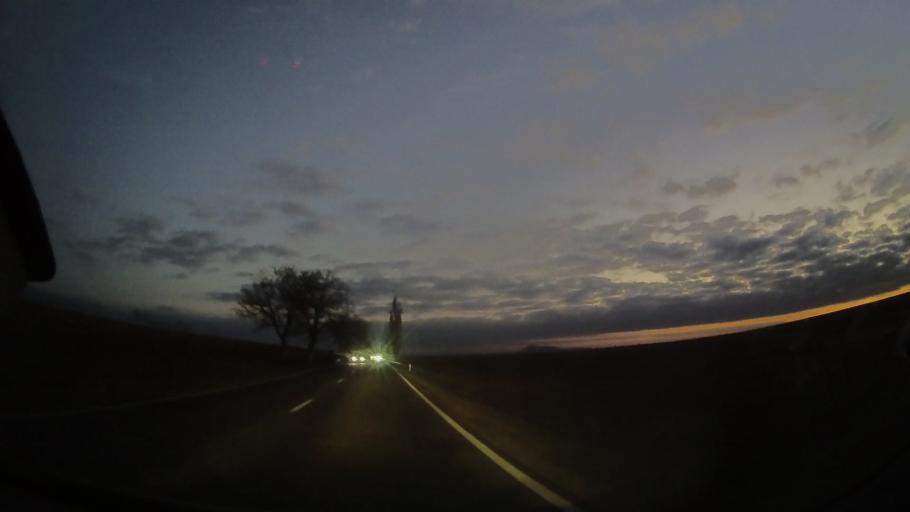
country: RO
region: Tulcea
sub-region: Comuna Frecatei
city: Cataloi
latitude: 45.0889
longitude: 28.7409
